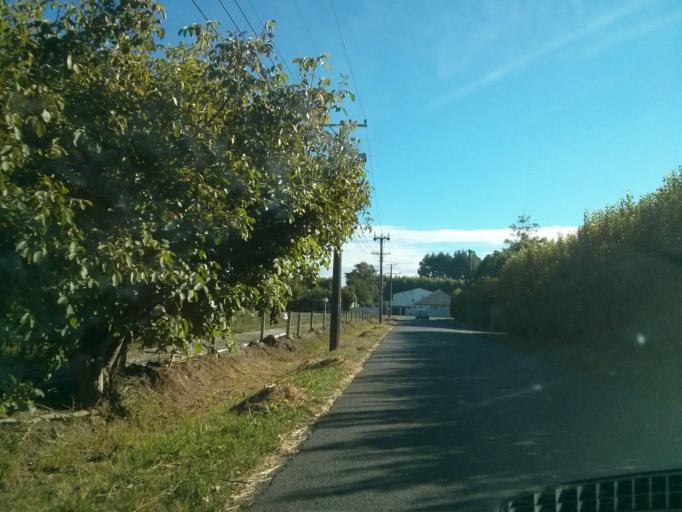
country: NZ
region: Canterbury
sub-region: Christchurch City
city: Christchurch
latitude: -43.4807
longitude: 172.5621
